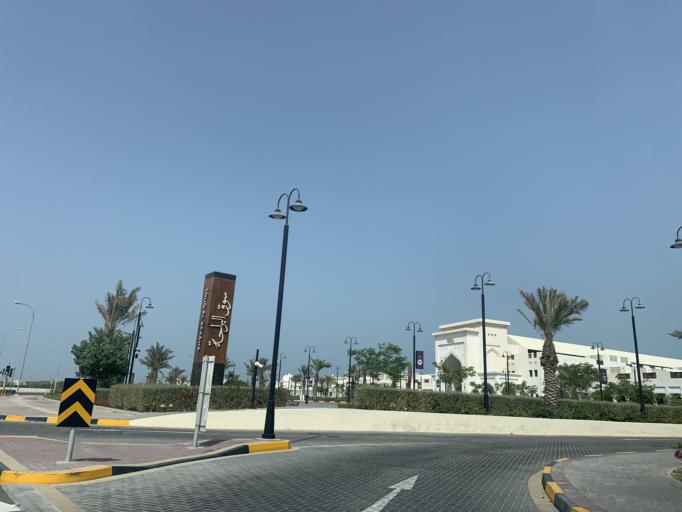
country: BH
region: Muharraq
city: Al Muharraq
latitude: 26.3048
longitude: 50.6355
